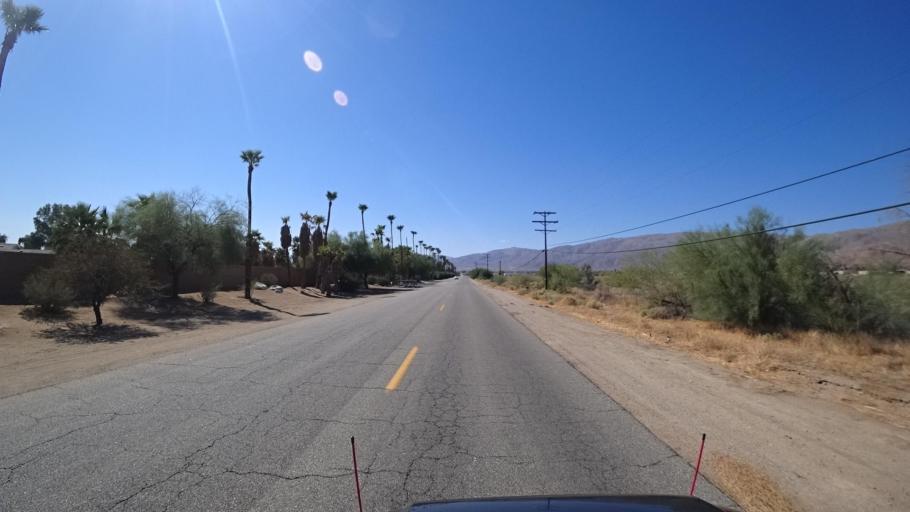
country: US
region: California
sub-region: San Diego County
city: Borrego Springs
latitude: 33.2641
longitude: -116.3661
